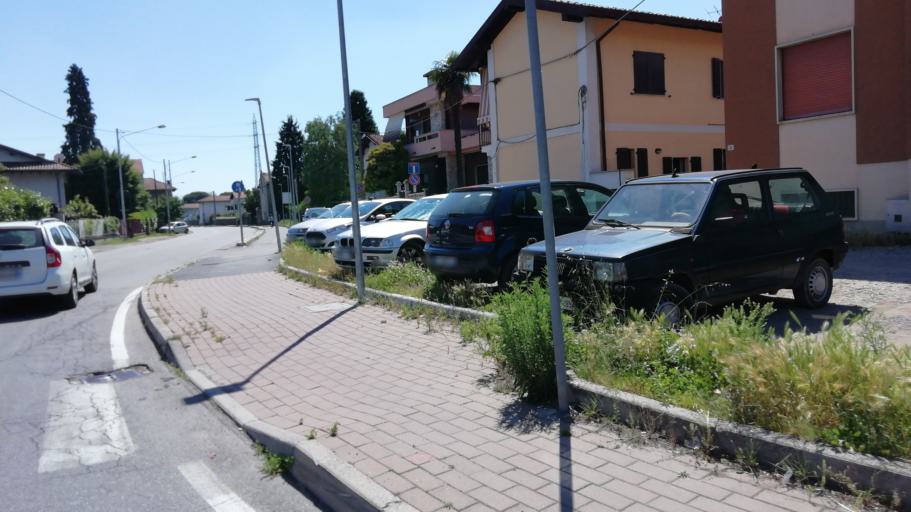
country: IT
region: Lombardy
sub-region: Provincia di Varese
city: Ferno
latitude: 45.6109
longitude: 8.7560
